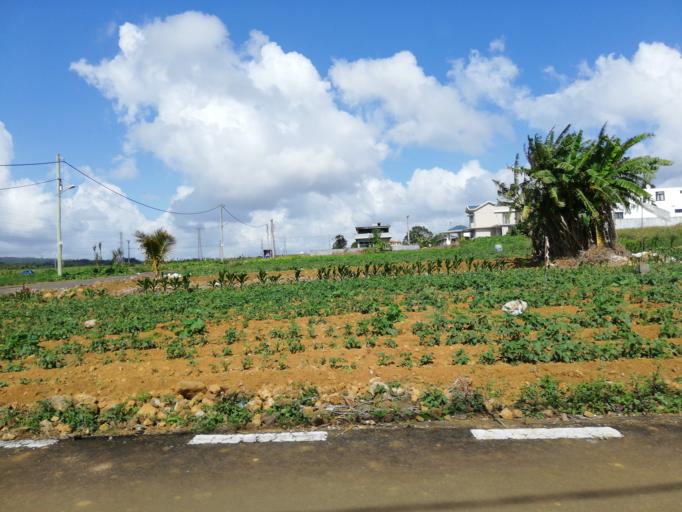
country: MU
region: Moka
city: Verdun
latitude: -20.2148
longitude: 57.5516
